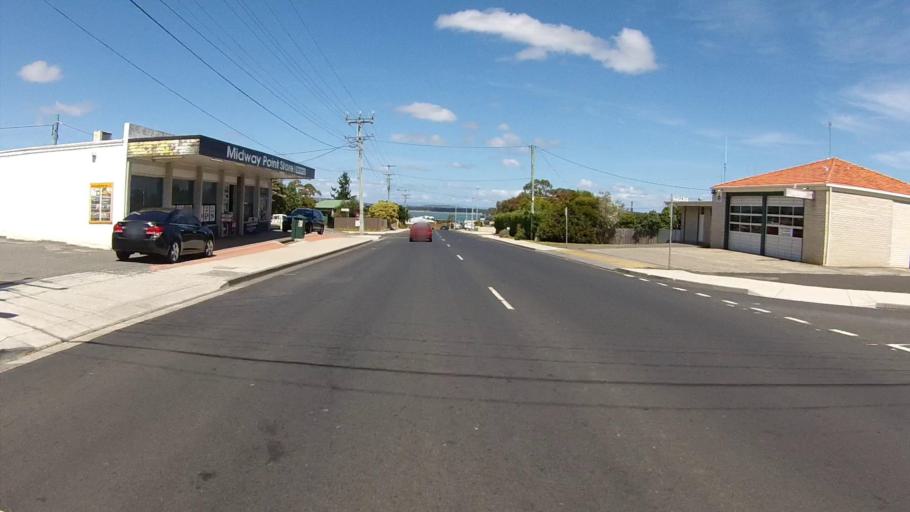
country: AU
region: Tasmania
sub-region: Sorell
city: Sorell
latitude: -42.8022
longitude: 147.5308
